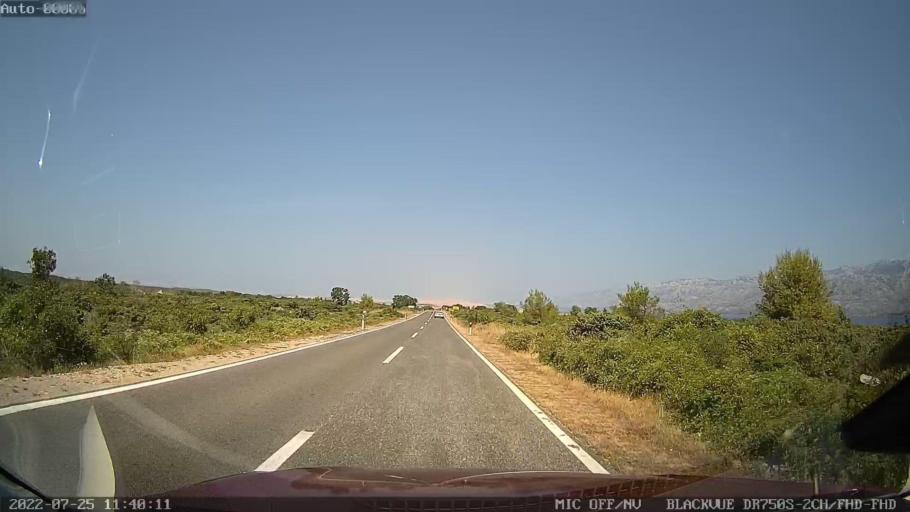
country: HR
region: Zadarska
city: Razanac
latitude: 44.2615
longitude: 15.3636
